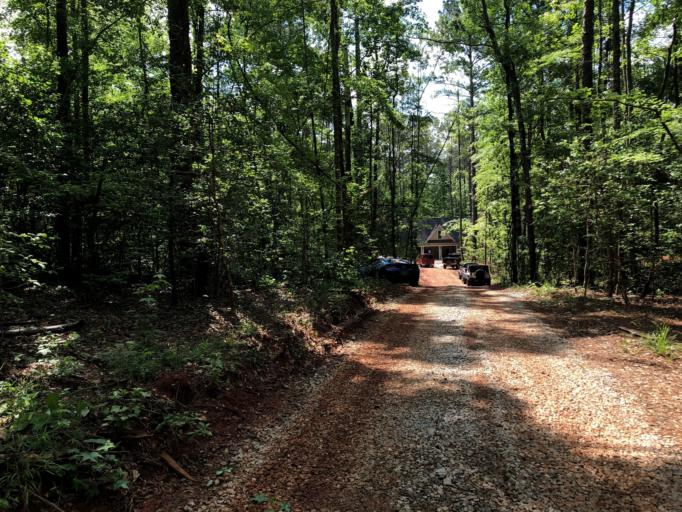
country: US
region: Georgia
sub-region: Troup County
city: La Grange
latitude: 33.1050
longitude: -85.0529
